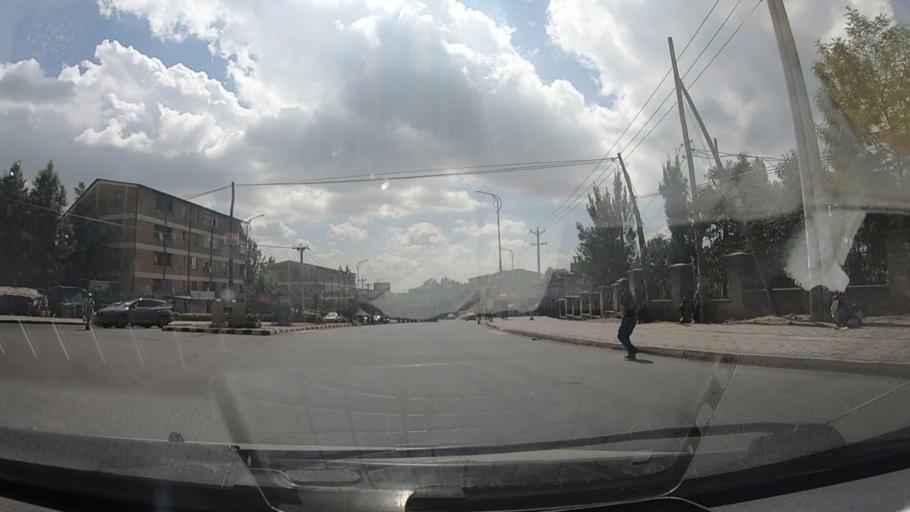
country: ET
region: Adis Abeba
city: Addis Ababa
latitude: 8.9782
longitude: 38.7218
